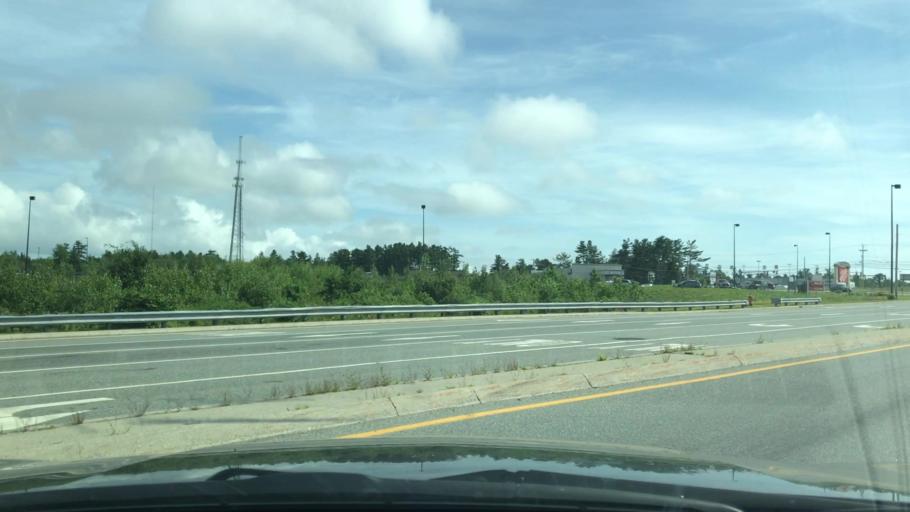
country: US
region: Maine
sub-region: Hancock County
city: Ellsworth
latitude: 44.5266
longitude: -68.3969
